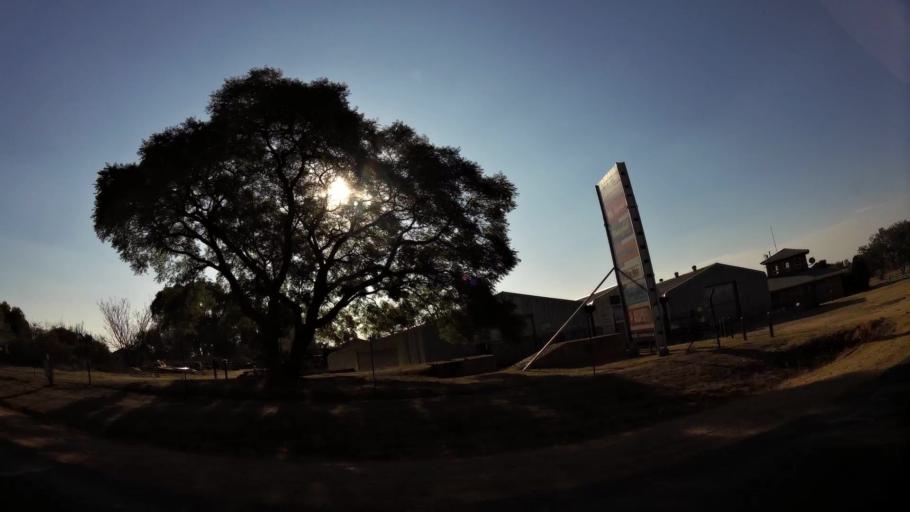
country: ZA
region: Gauteng
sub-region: West Rand District Municipality
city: Muldersdriseloop
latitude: -26.0127
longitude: 27.8907
